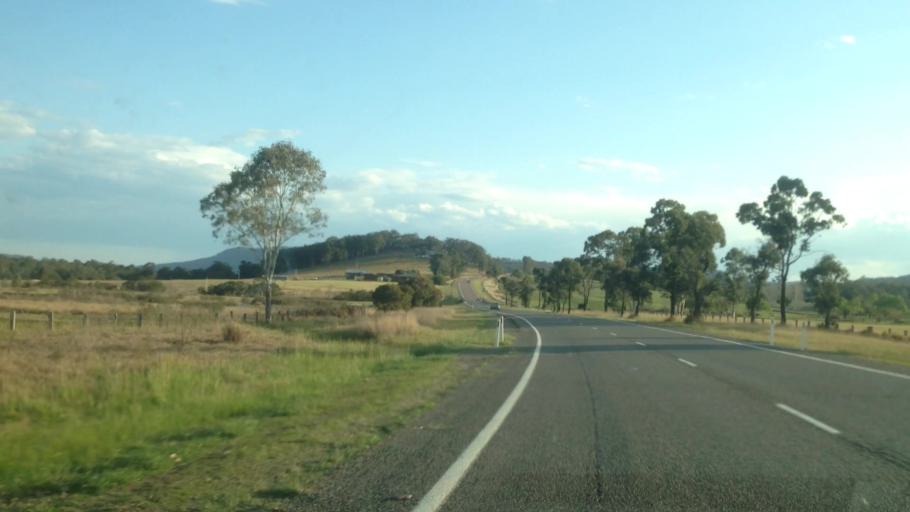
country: AU
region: New South Wales
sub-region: Cessnock
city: Kurri Kurri
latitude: -32.8753
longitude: 151.4754
